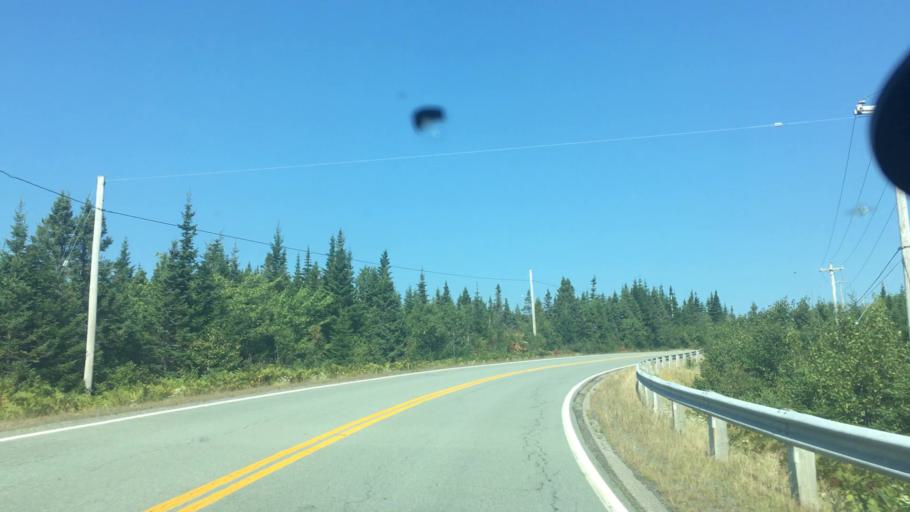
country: CA
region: Nova Scotia
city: Antigonish
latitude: 45.0079
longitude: -62.1056
